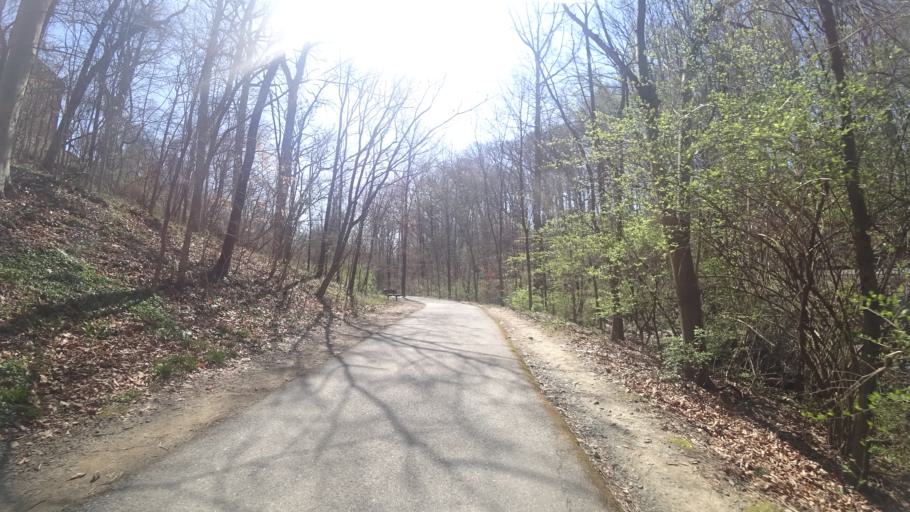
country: US
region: Maryland
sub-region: Montgomery County
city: Takoma Park
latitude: 38.9845
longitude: -77.0025
